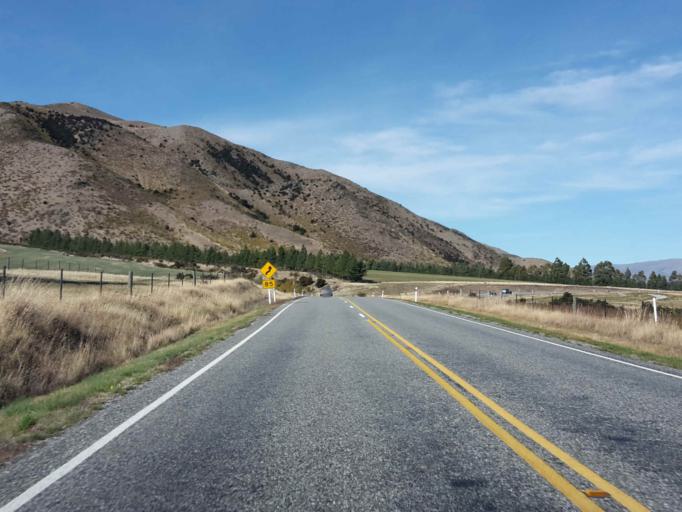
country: NZ
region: Otago
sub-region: Queenstown-Lakes District
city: Wanaka
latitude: -44.7480
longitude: 169.3443
